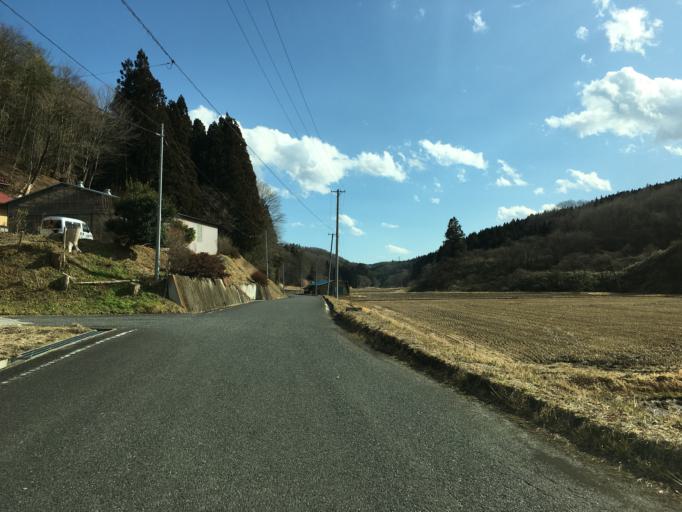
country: JP
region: Fukushima
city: Ishikawa
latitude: 37.2357
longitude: 140.5905
